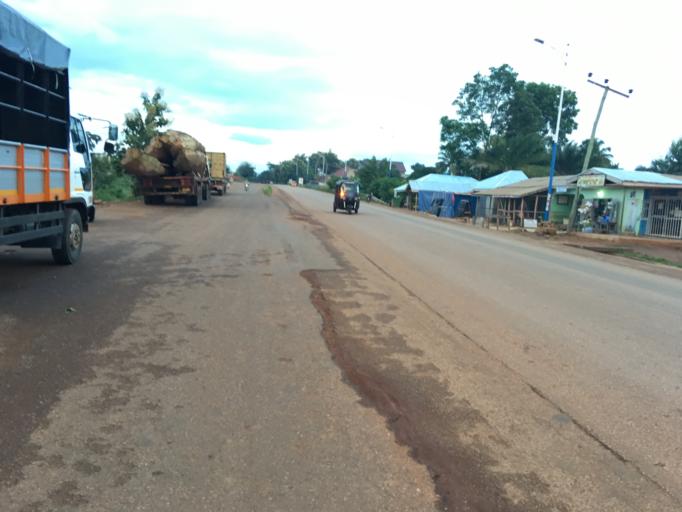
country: GH
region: Western
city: Bibiani
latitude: 6.7892
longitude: -2.5166
